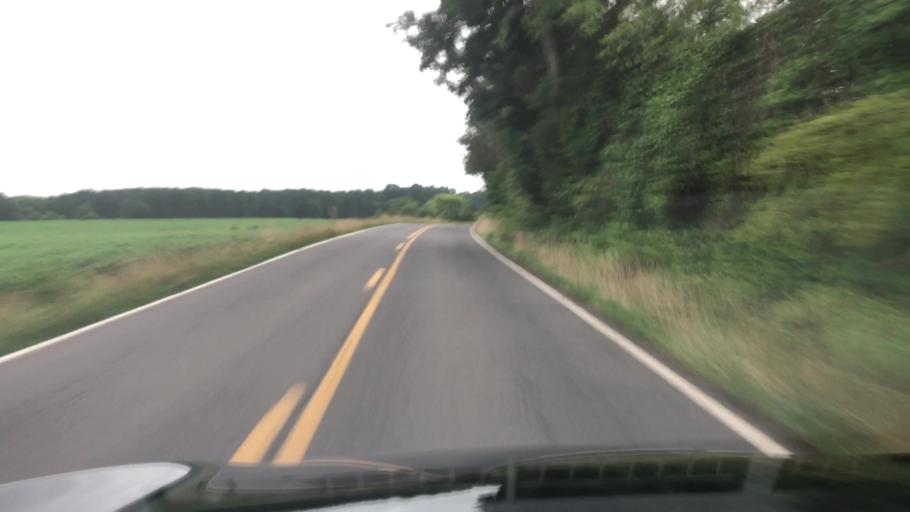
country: US
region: Virginia
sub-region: Prince William County
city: Nokesville
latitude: 38.5783
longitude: -77.6133
